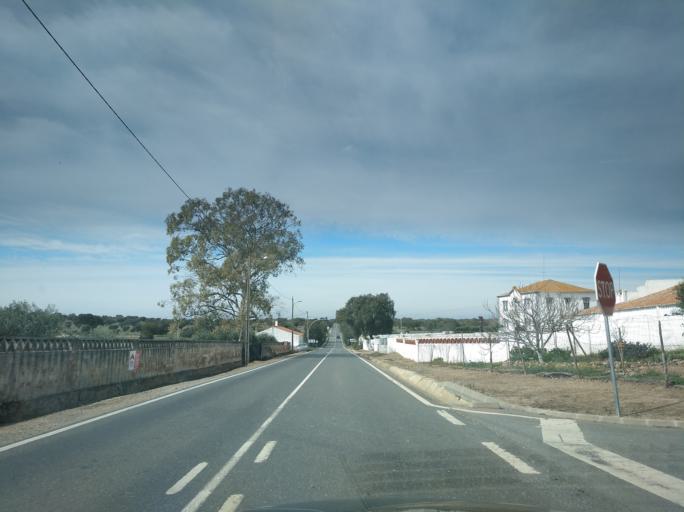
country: PT
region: Beja
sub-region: Mertola
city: Mertola
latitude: 37.7442
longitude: -7.7941
